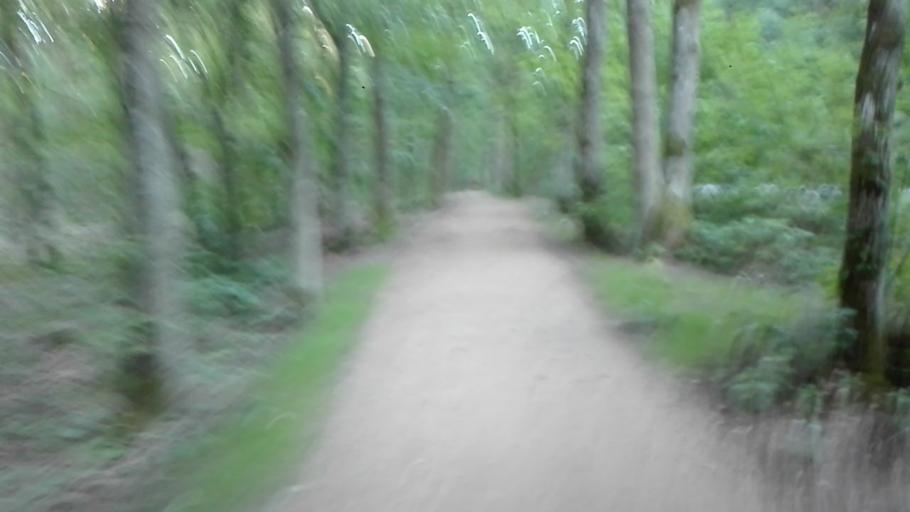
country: PL
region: West Pomeranian Voivodeship
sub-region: Powiat policki
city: Dobra
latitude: 53.4783
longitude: 14.3628
